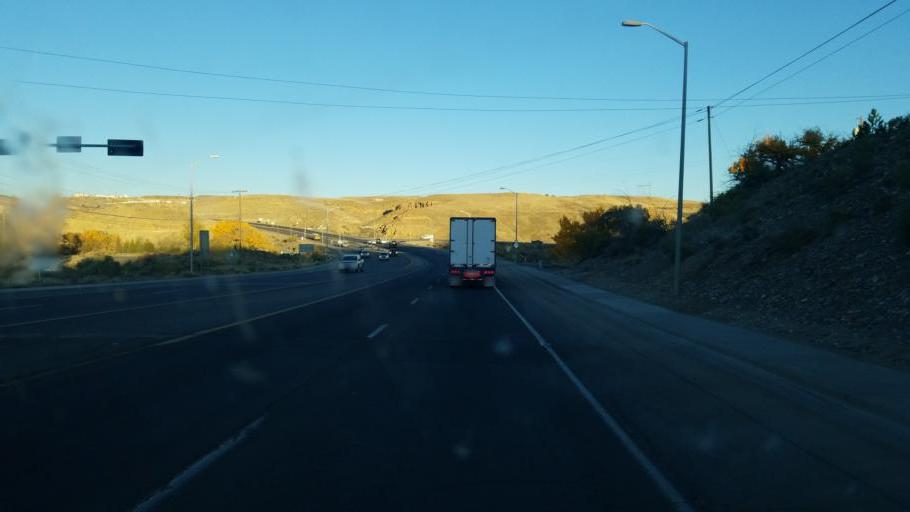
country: US
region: New Mexico
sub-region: San Juan County
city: Farmington
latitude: 36.7363
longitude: -108.2488
